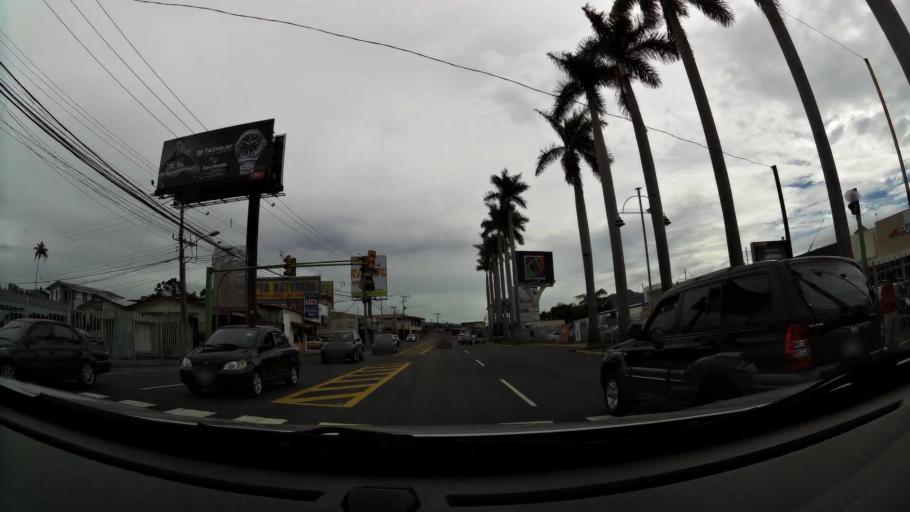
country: CR
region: San Jose
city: San Pedro
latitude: 9.9186
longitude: -84.0473
